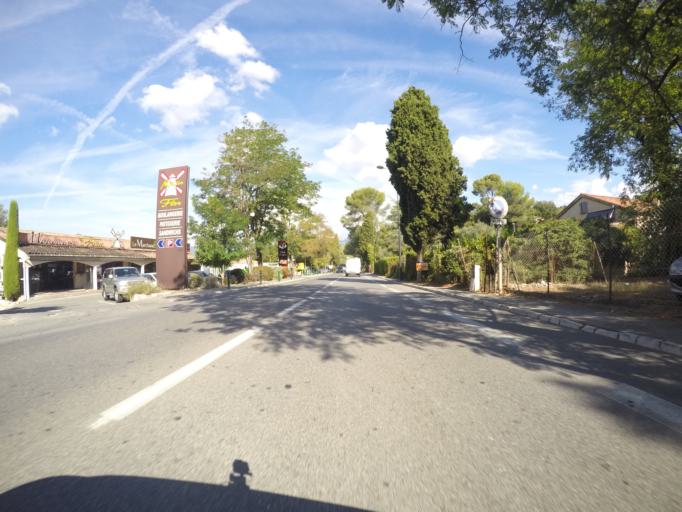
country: FR
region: Provence-Alpes-Cote d'Azur
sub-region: Departement des Alpes-Maritimes
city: Le Rouret
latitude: 43.6629
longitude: 7.0560
